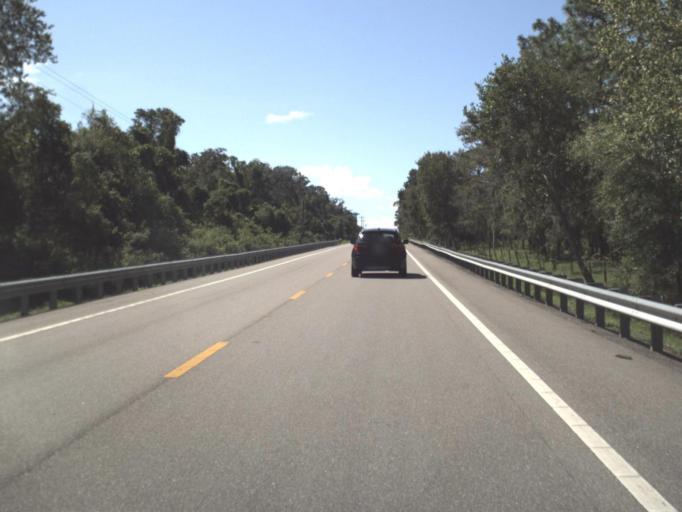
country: US
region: Florida
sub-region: Sarasota County
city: Lake Sarasota
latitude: 27.3872
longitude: -82.2628
